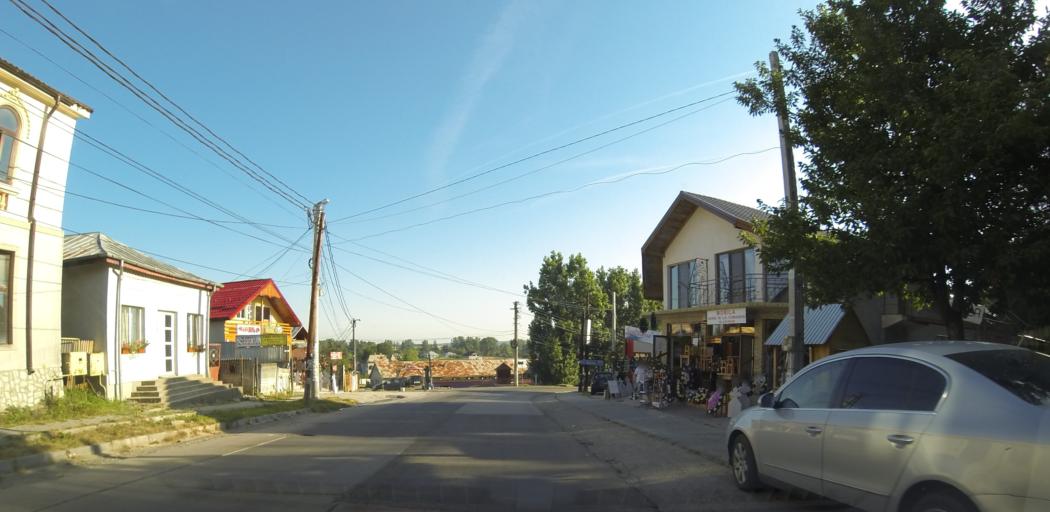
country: RO
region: Valcea
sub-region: Comuna Balcesti
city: Balcesti
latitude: 44.6183
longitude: 23.9390
